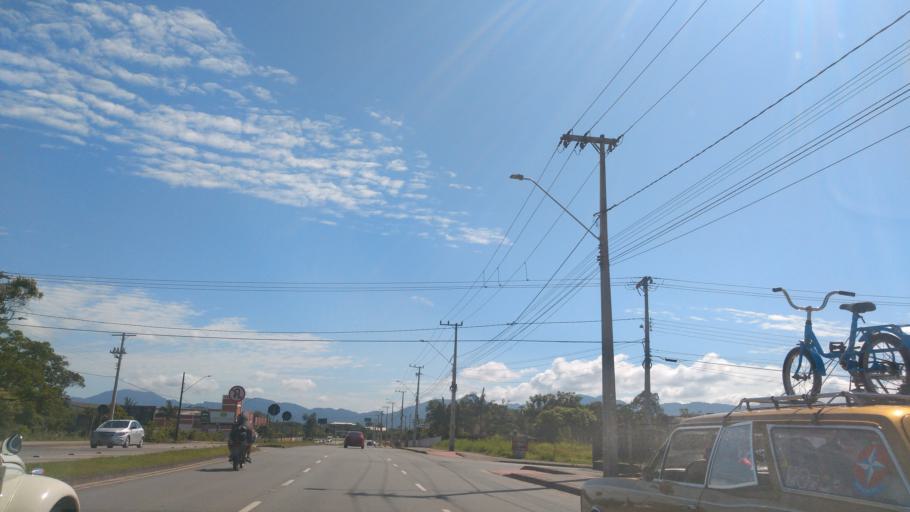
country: BR
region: Santa Catarina
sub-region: Joinville
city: Joinville
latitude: -26.2301
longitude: -48.8064
